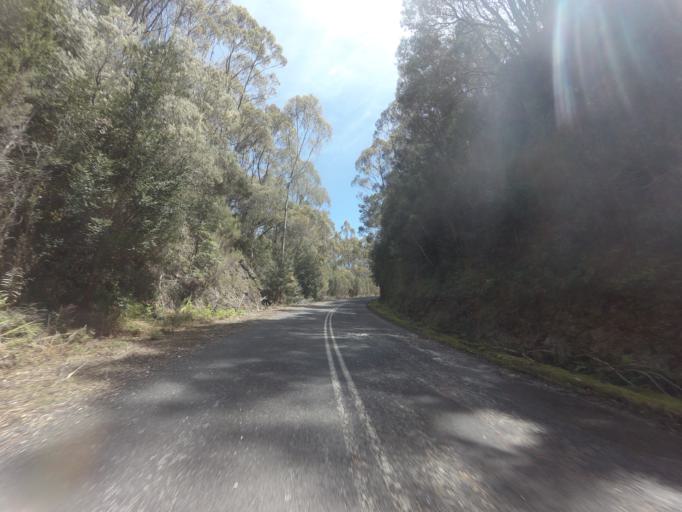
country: AU
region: Tasmania
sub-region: Huon Valley
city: Geeveston
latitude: -42.8213
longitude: 146.1084
